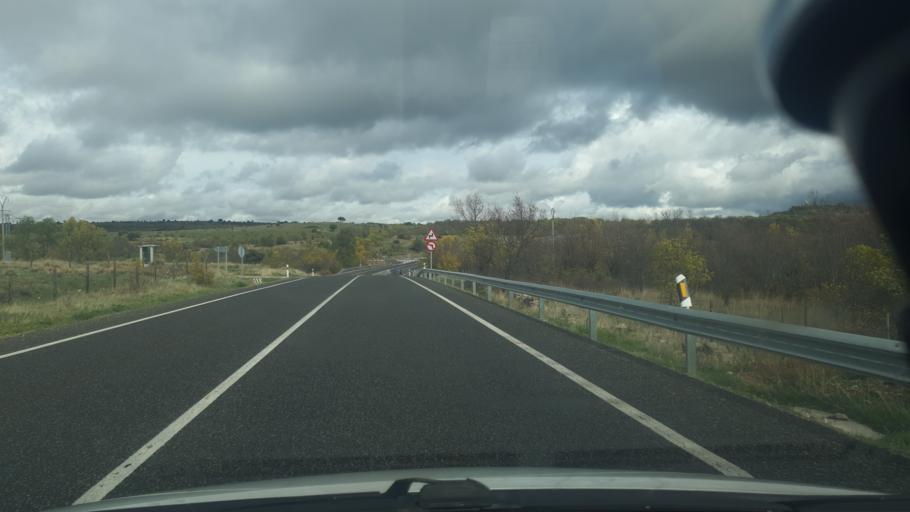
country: ES
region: Castille and Leon
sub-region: Provincia de Segovia
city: Gallegos
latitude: 41.0752
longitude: -3.8066
